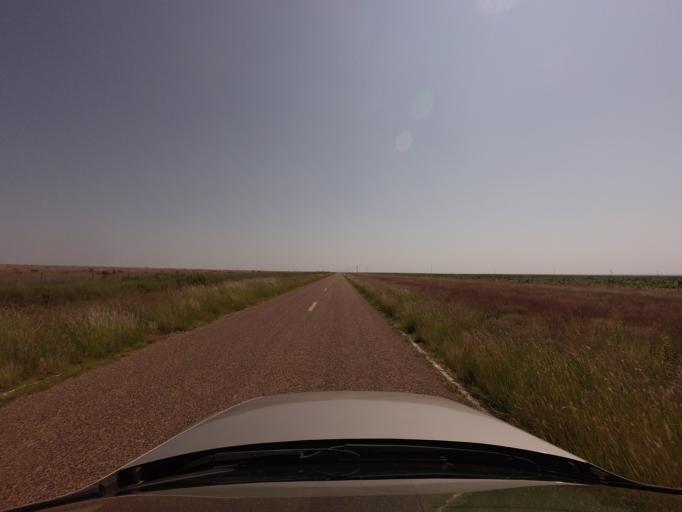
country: US
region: New Mexico
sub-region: Curry County
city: Cannon Air Force Base
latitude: 34.6330
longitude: -103.3945
